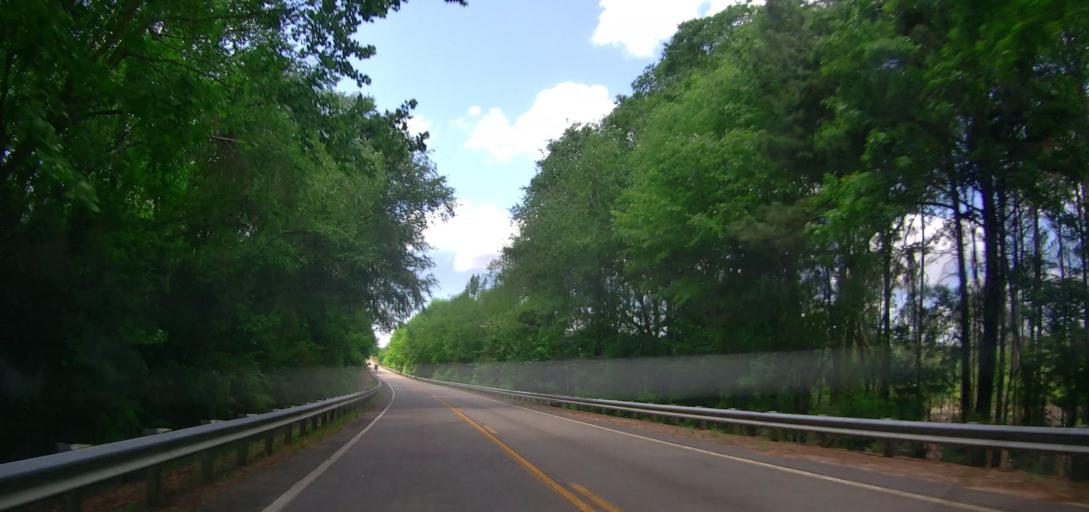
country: US
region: Georgia
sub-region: Dodge County
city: Chester
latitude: 32.5370
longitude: -83.1972
